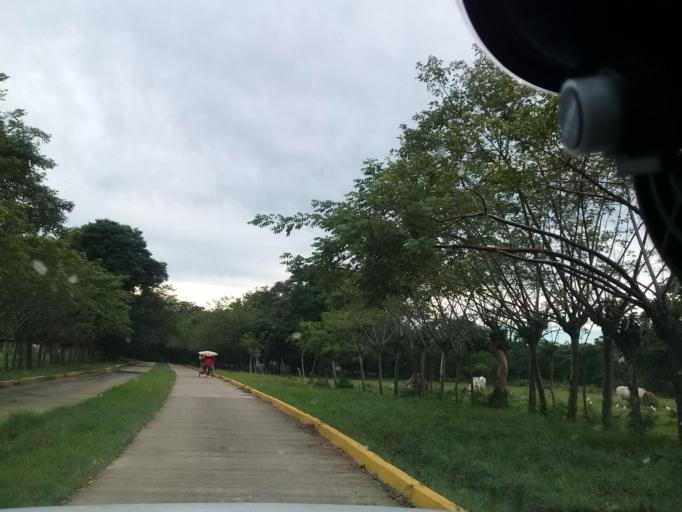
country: MX
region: Hidalgo
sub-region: Huejutla de Reyes
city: Chalahuiyapa
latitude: 21.1621
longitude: -98.3622
